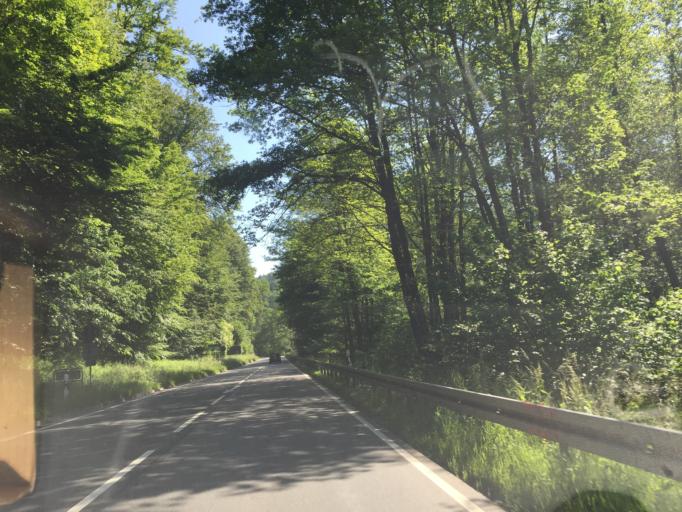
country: DE
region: Hesse
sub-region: Regierungsbezirk Darmstadt
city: Beerfelden
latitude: 49.6074
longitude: 8.9886
